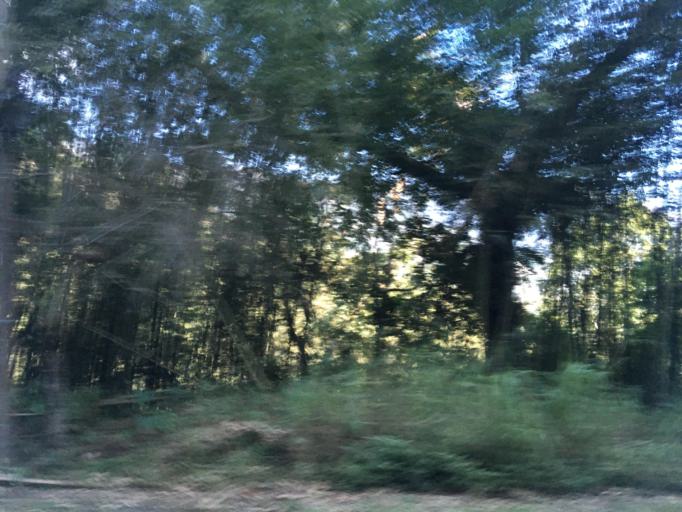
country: TW
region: Taiwan
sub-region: Chiayi
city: Jiayi Shi
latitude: 23.4705
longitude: 120.6958
